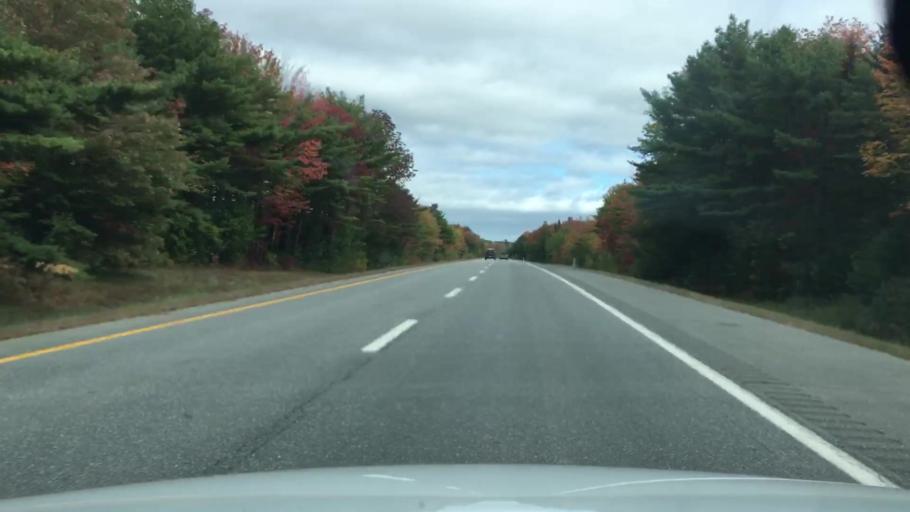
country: US
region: Maine
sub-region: Penobscot County
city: Carmel
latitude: 44.7737
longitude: -69.0300
